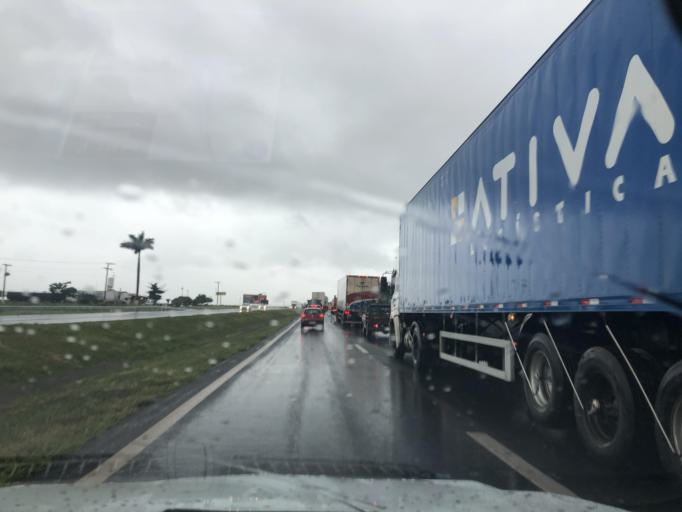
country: BR
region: Sao Paulo
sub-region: Porto Ferreira
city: Porto Ferreira
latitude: -21.8043
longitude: -47.5039
